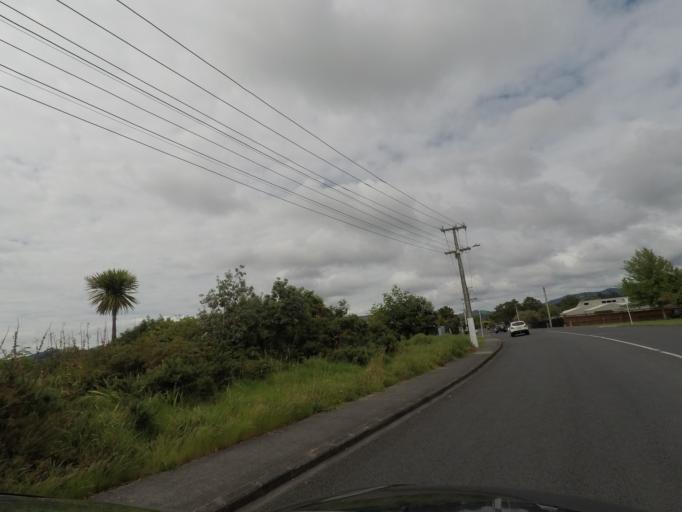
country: NZ
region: Auckland
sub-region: Auckland
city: Waitakere
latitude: -36.9003
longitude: 174.6226
